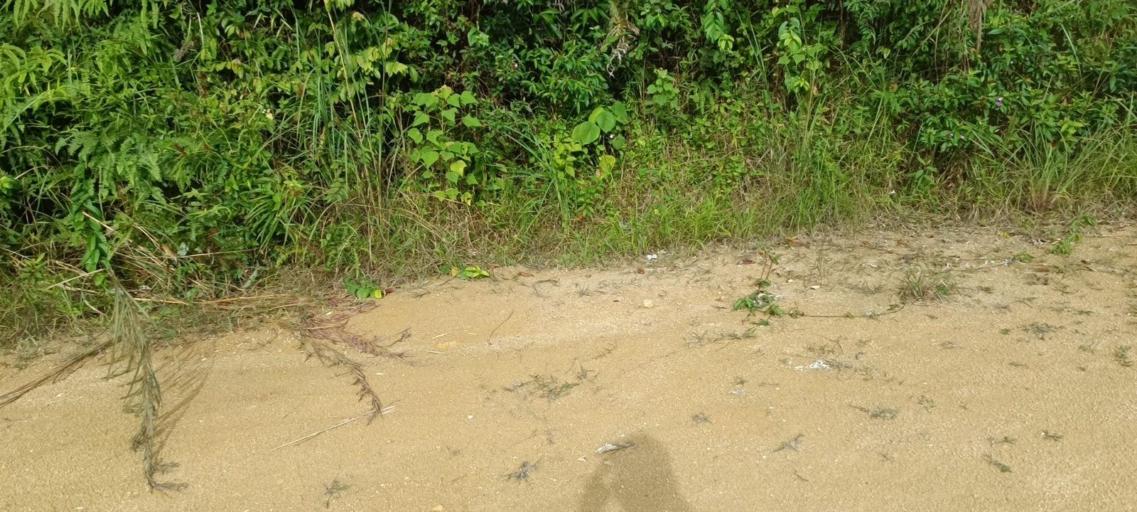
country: MY
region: Penang
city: Nibong Tebal
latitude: 5.2297
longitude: 100.5142
